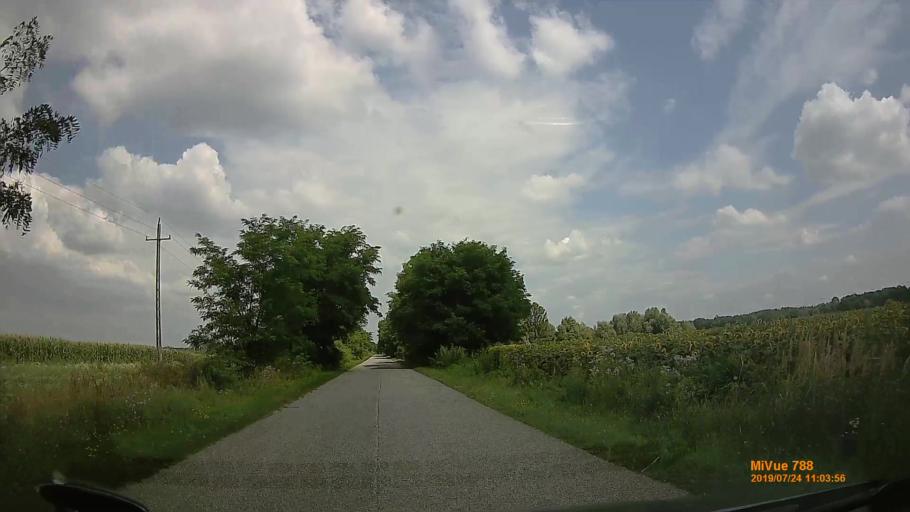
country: HU
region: Szabolcs-Szatmar-Bereg
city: Tarpa
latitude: 48.1643
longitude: 22.5161
